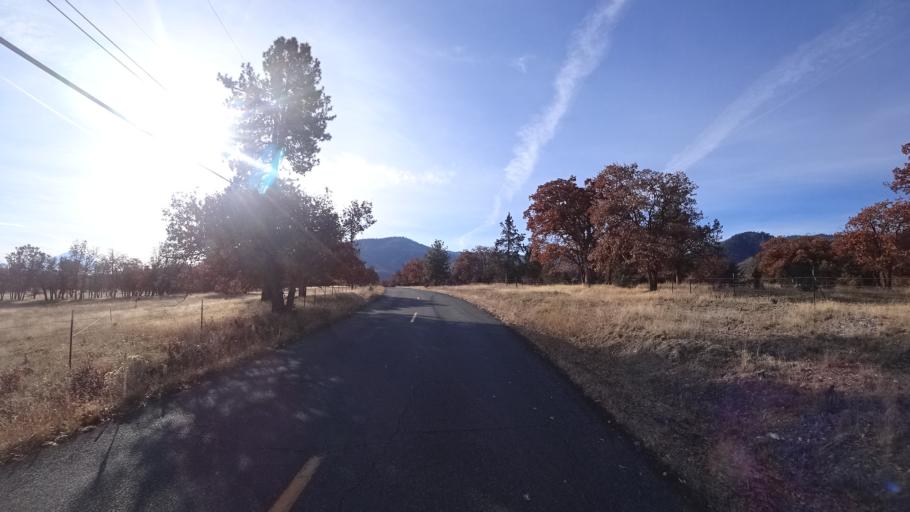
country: US
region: California
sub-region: Siskiyou County
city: Yreka
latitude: 41.6711
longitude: -122.6233
